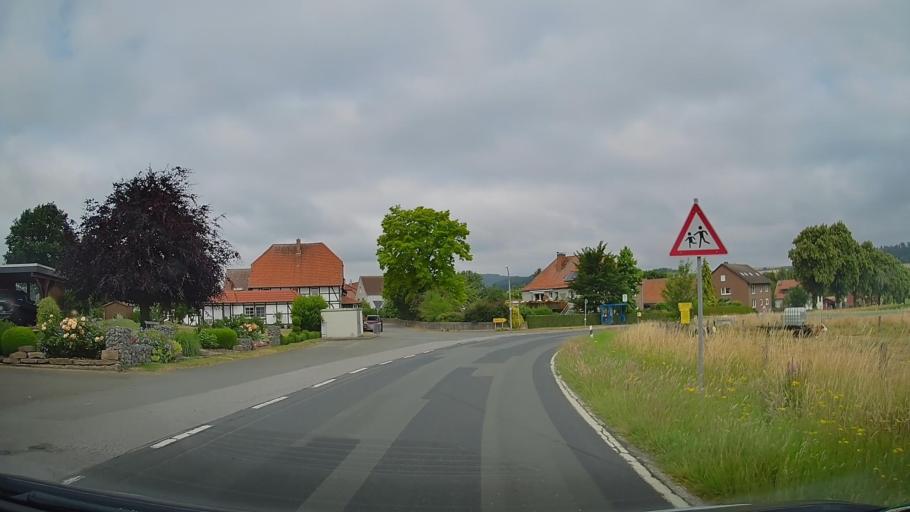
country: DE
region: Lower Saxony
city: Aerzen
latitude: 52.0347
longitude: 9.1990
